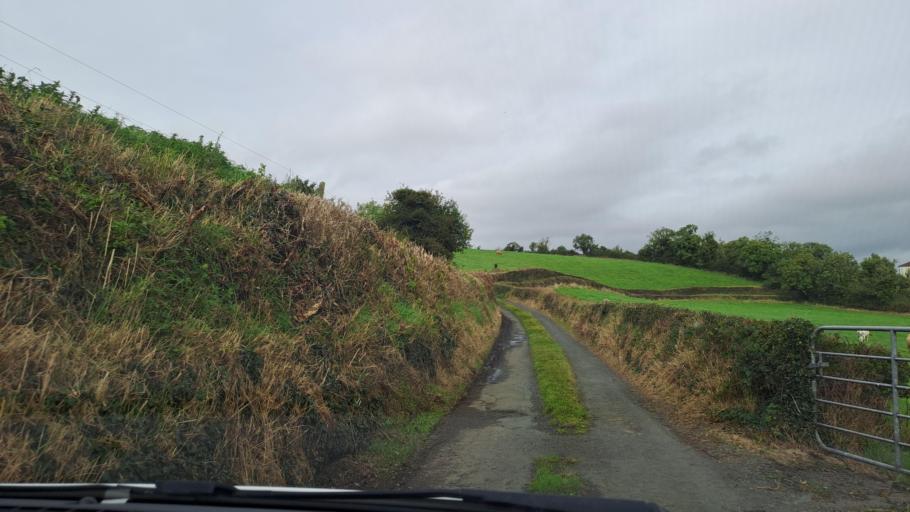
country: IE
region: Ulster
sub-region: An Cabhan
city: Bailieborough
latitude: 53.9967
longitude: -6.9384
